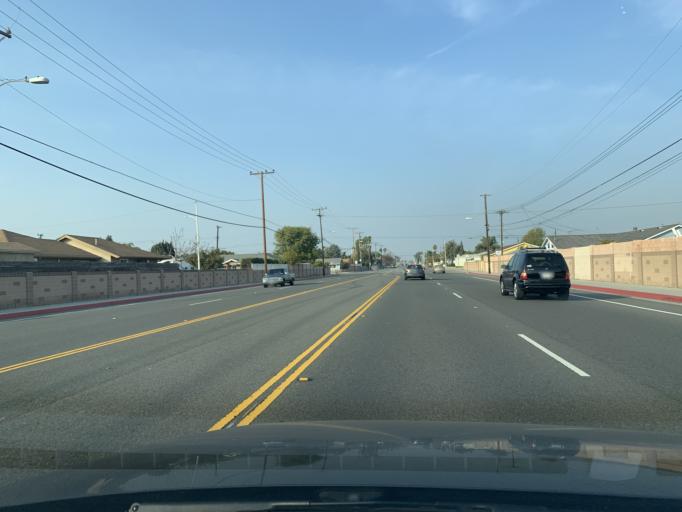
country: US
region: California
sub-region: Orange County
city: Westminster
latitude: 33.7530
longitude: -118.0245
